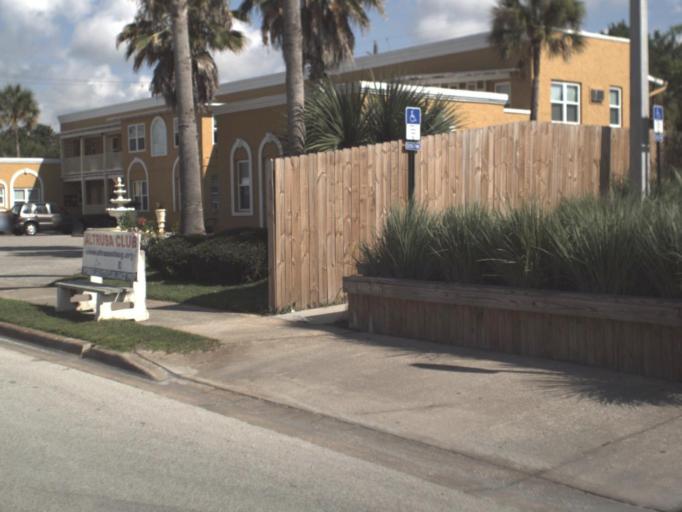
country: US
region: Florida
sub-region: Saint Johns County
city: Saint Augustine
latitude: 29.8910
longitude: -81.2968
